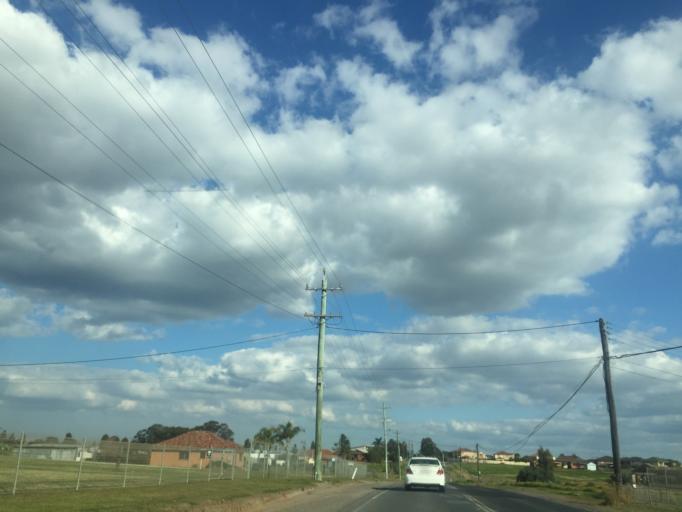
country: AU
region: New South Wales
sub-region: Blacktown
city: Quakers Hill
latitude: -33.7096
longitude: 150.8936
